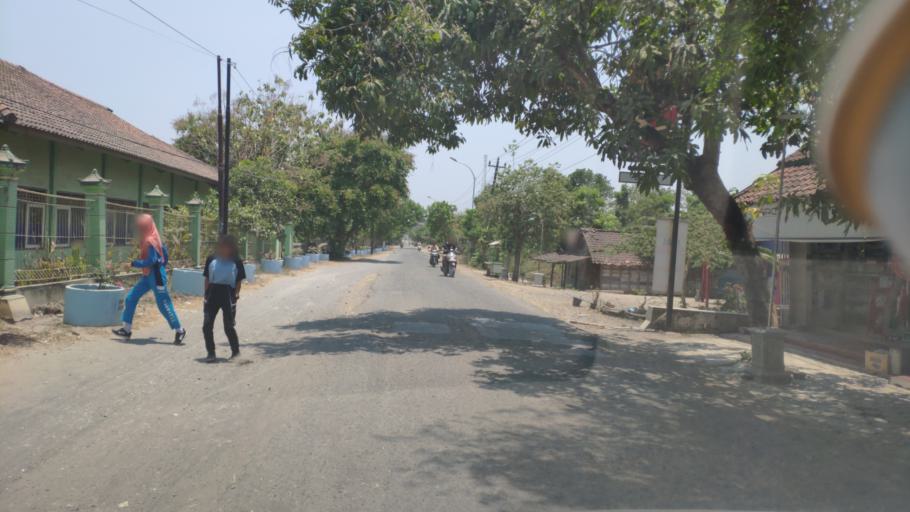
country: ID
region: Central Java
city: Mendenrejo
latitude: -7.2430
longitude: 111.4494
